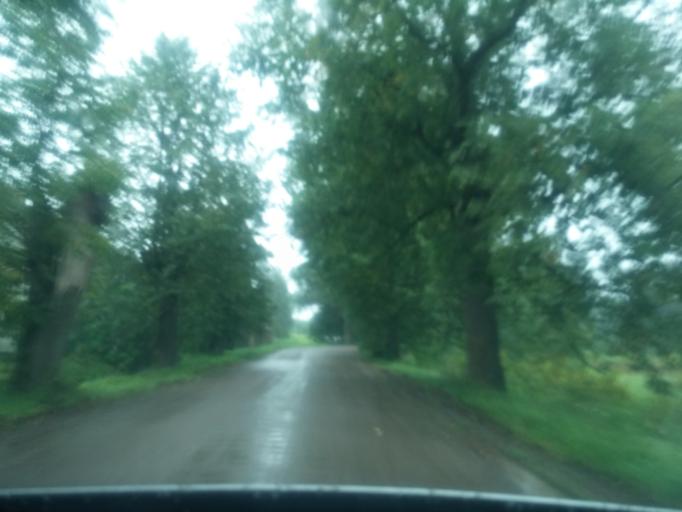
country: LV
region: Ogre
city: Ogre
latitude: 56.8660
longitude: 24.5757
